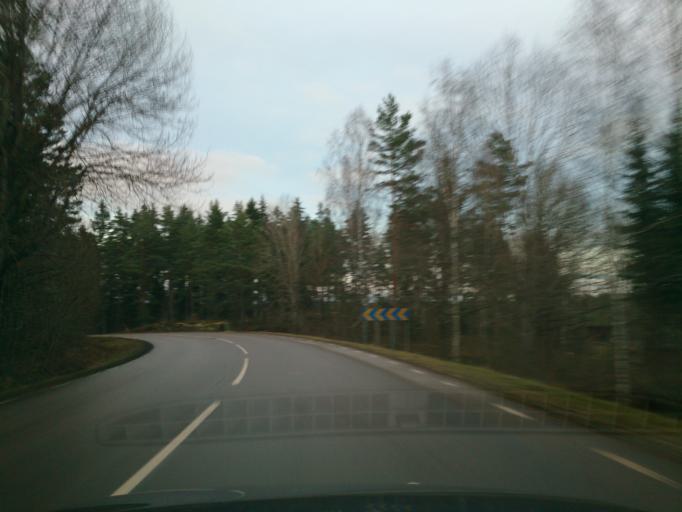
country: SE
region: OEstergoetland
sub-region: Norrkopings Kommun
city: Kimstad
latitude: 58.3757
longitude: 16.0282
